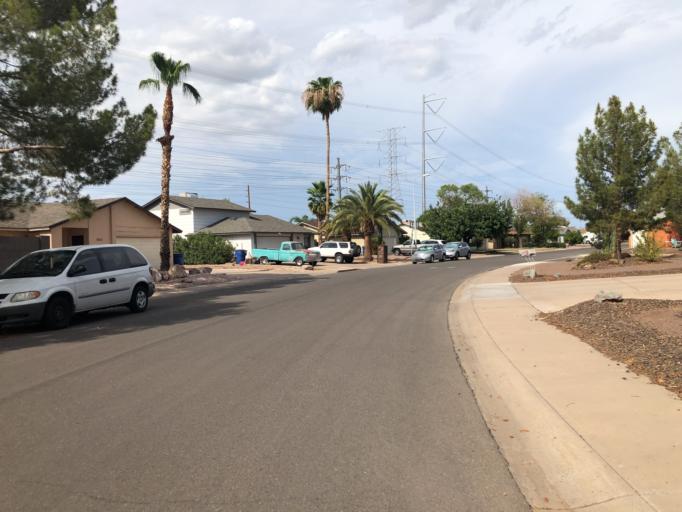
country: US
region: Arizona
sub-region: Maricopa County
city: San Carlos
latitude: 33.3559
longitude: -111.8754
